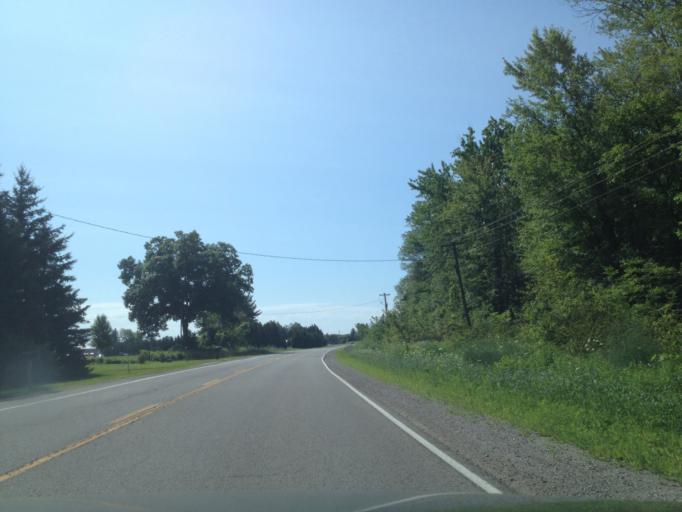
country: CA
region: Ontario
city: Norfolk County
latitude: 42.7909
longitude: -80.4088
